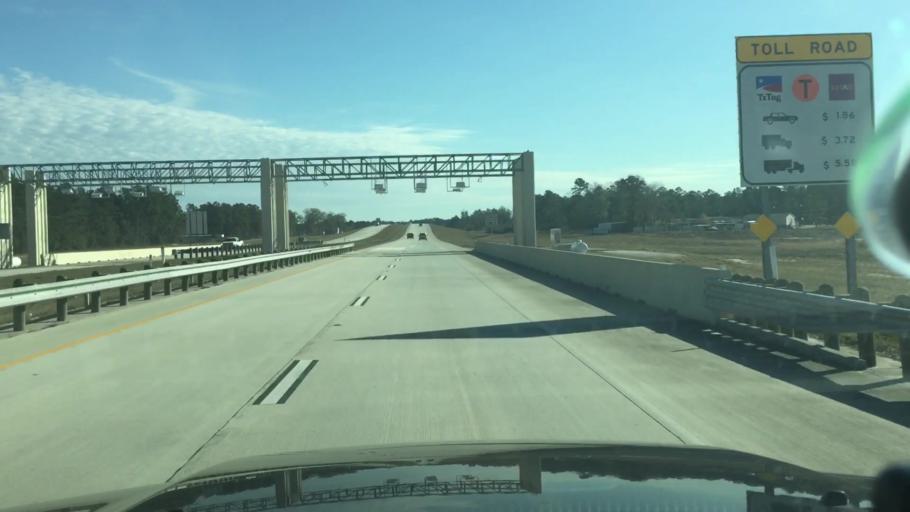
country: US
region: Texas
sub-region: Montgomery County
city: Porter Heights
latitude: 30.1376
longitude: -95.2790
